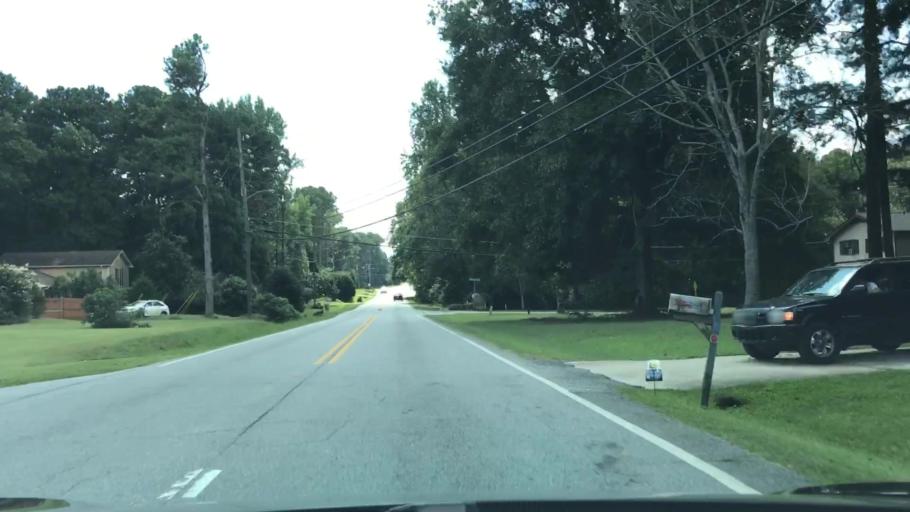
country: US
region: Georgia
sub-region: Gwinnett County
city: Lawrenceville
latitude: 33.9438
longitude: -84.0616
